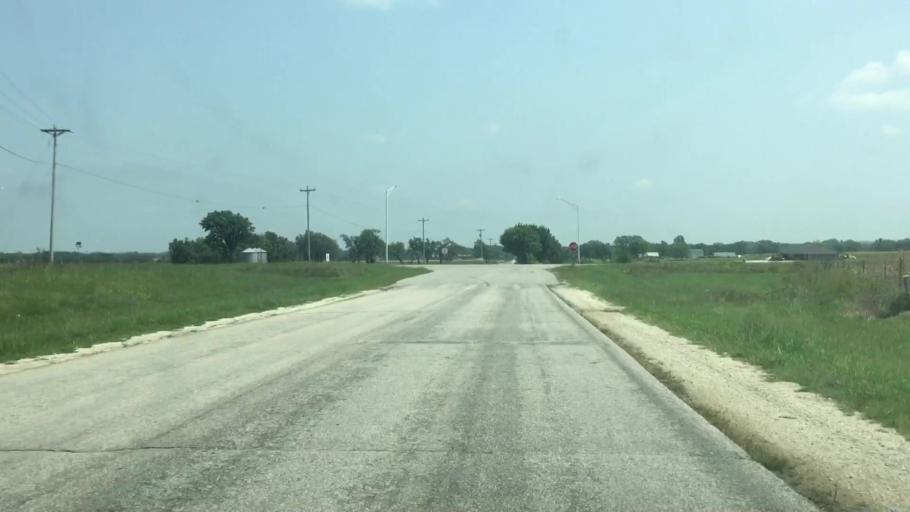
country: US
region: Kansas
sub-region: Allen County
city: Iola
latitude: 37.9512
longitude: -95.3825
